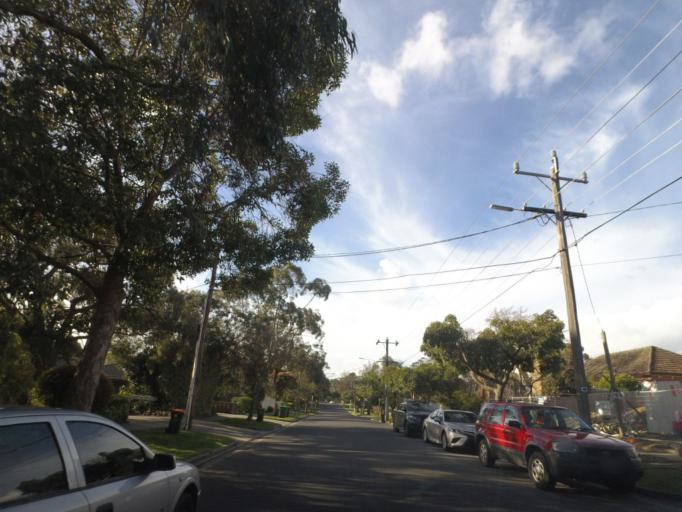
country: AU
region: Victoria
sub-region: Whitehorse
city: Blackburn
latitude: -37.8296
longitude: 145.1487
